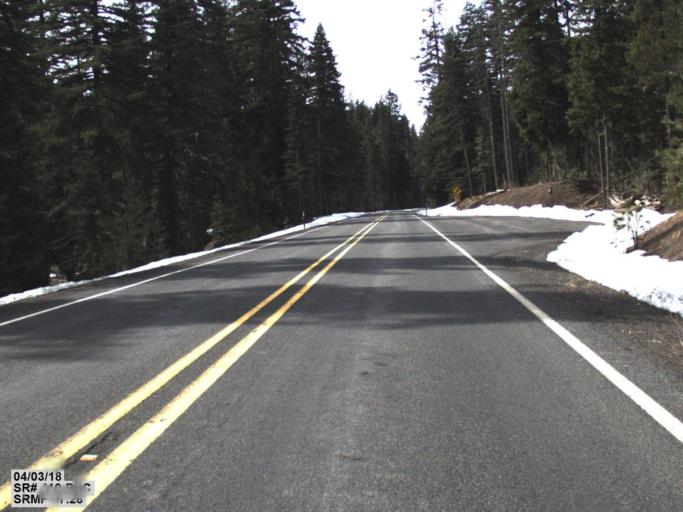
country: US
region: Washington
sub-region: Kittitas County
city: Cle Elum
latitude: 46.9739
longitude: -121.1902
